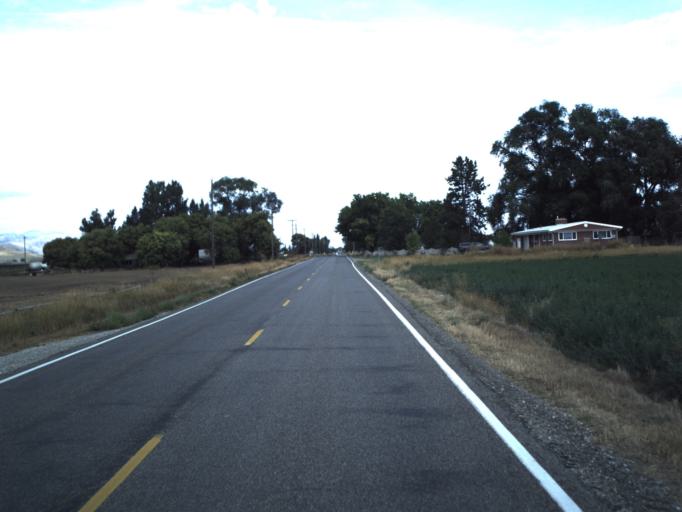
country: US
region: Utah
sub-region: Cache County
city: Lewiston
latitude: 41.9623
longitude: -111.9540
